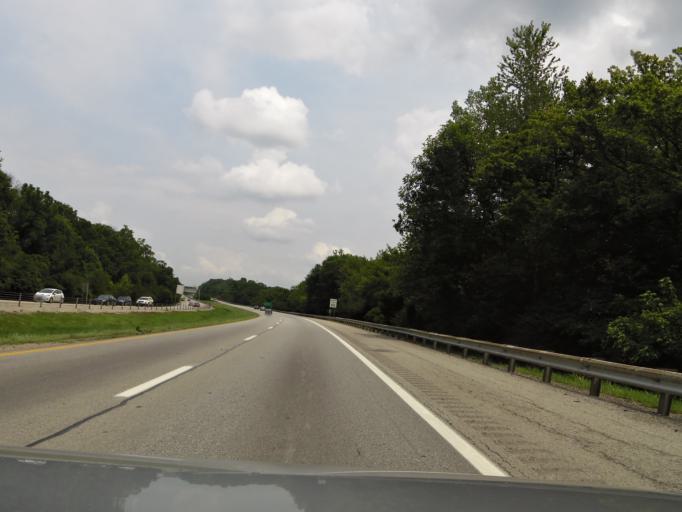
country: US
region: Kentucky
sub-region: Jefferson County
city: Northfield
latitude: 38.2939
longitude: -85.6320
